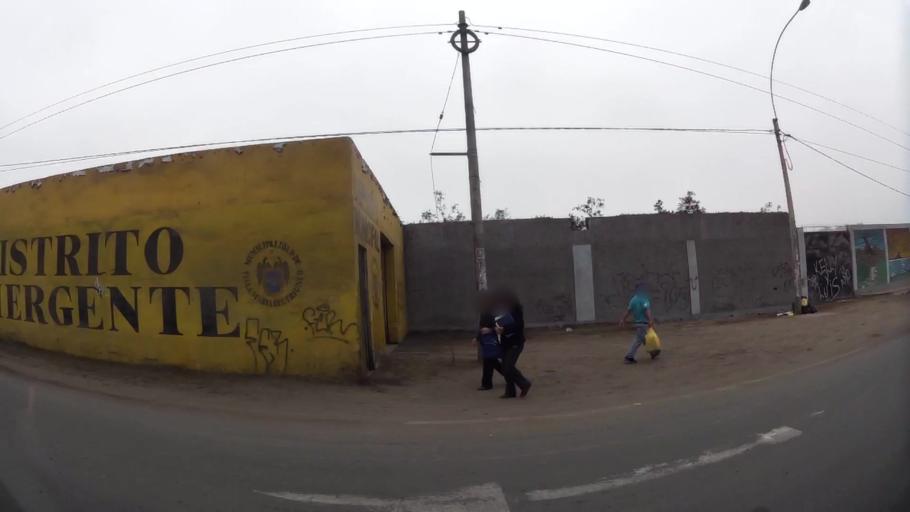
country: PE
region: Lima
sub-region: Lima
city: Surco
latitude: -12.1720
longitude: -76.9458
